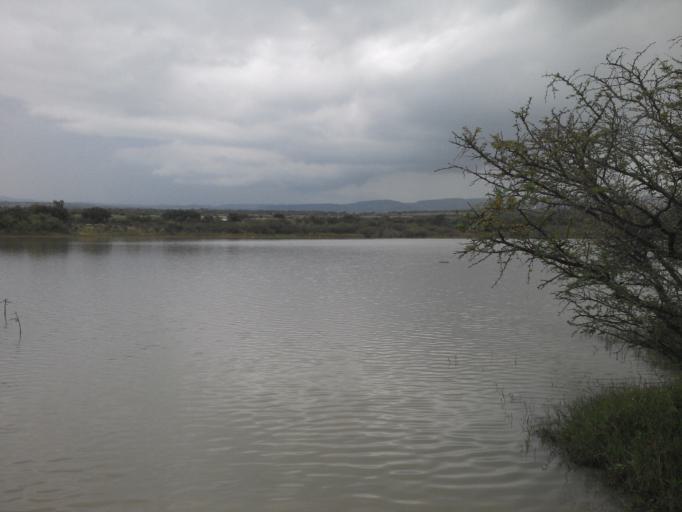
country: MX
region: Guanajuato
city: Ciudad Manuel Doblado
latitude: 20.8080
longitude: -102.0021
